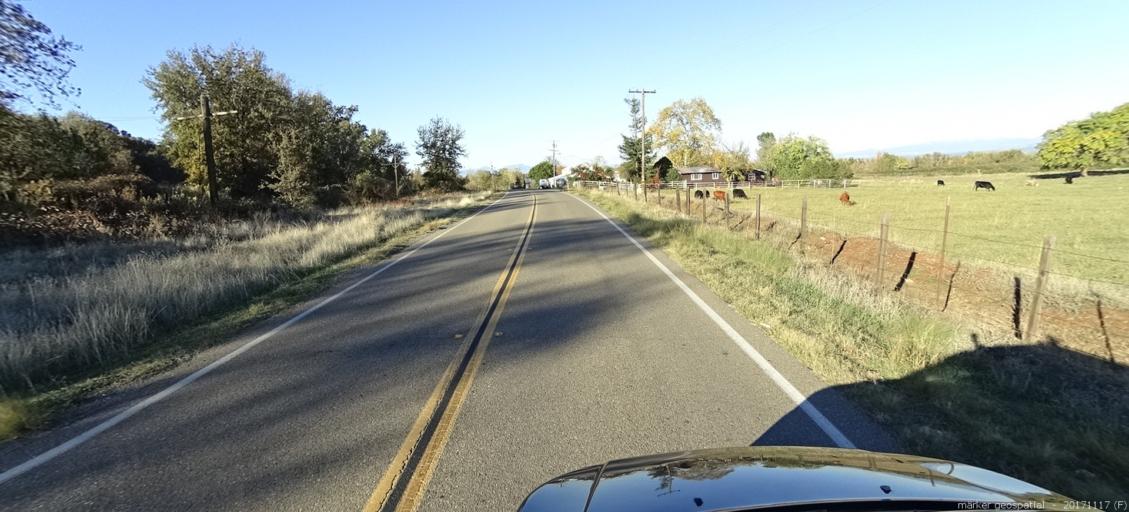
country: US
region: California
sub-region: Shasta County
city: Cottonwood
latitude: 40.4044
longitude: -122.2443
